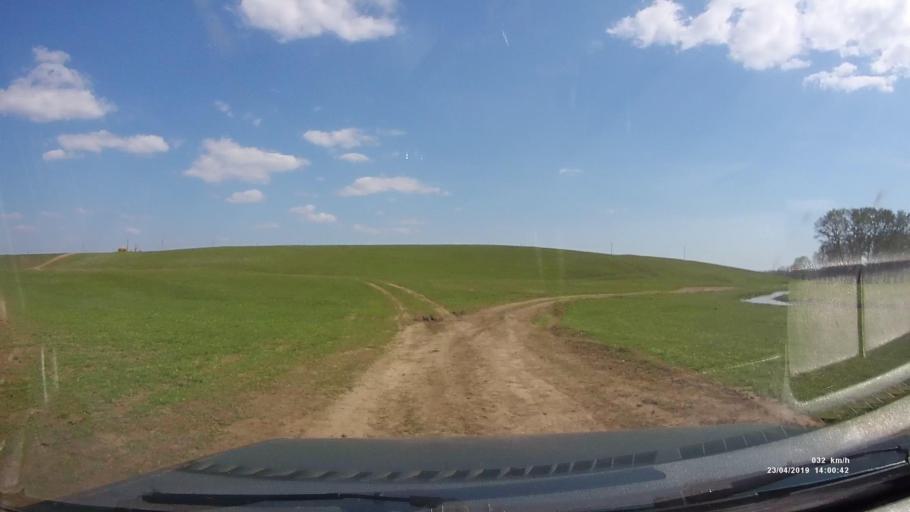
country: RU
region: Rostov
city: Remontnoye
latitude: 46.5582
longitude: 42.9471
